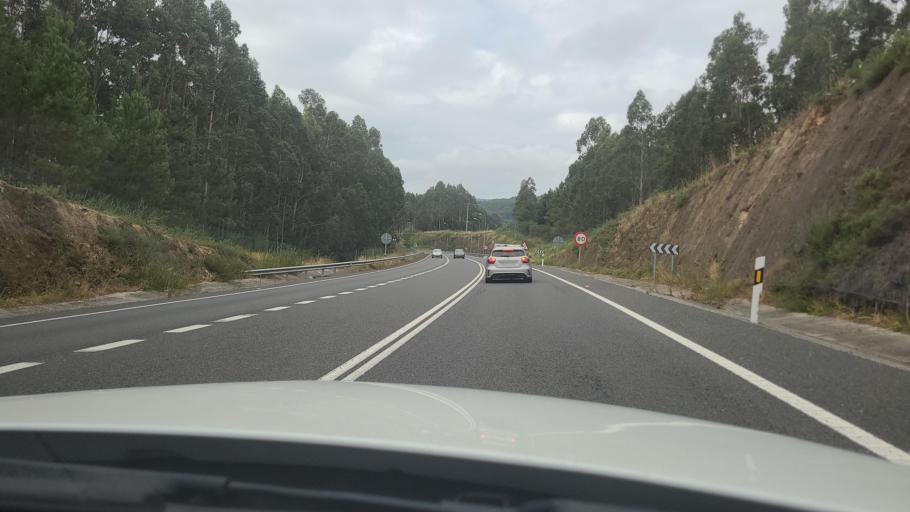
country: ES
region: Galicia
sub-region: Provincia da Coruna
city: Corcubion
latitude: 42.9466
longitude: -9.2227
